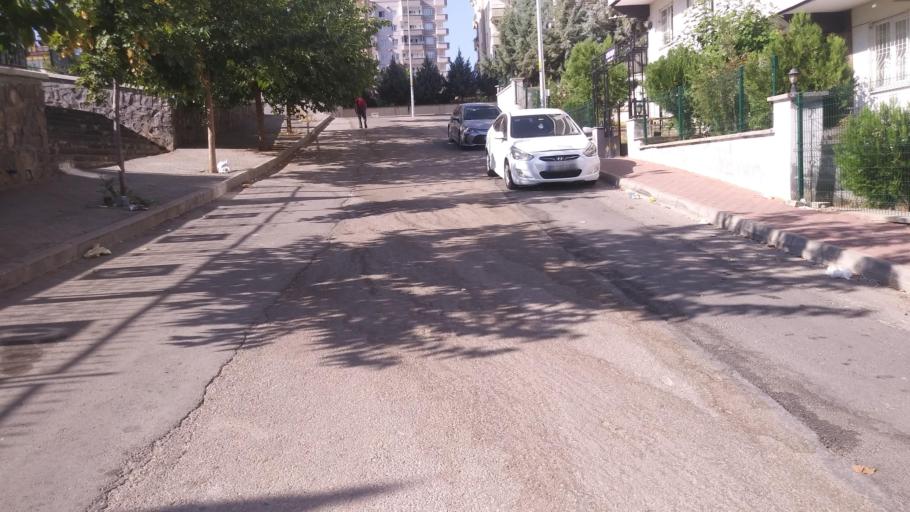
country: TR
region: Gaziantep
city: Sahinbey
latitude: 37.0307
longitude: 37.3353
